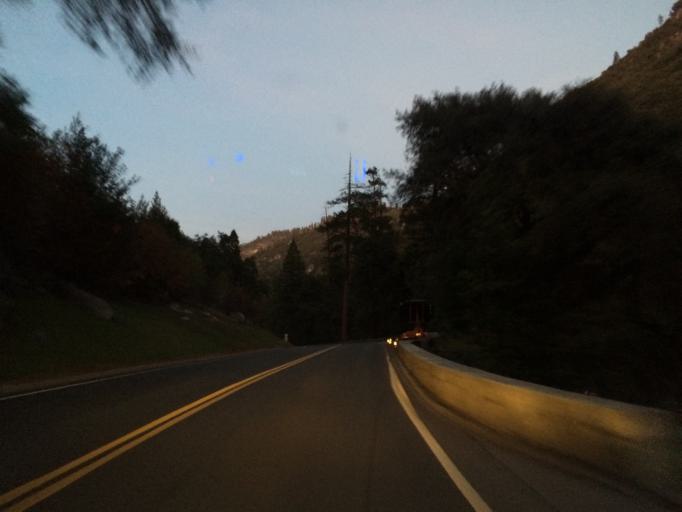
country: US
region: California
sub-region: Mariposa County
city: Yosemite Valley
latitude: 37.6794
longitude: -119.7356
